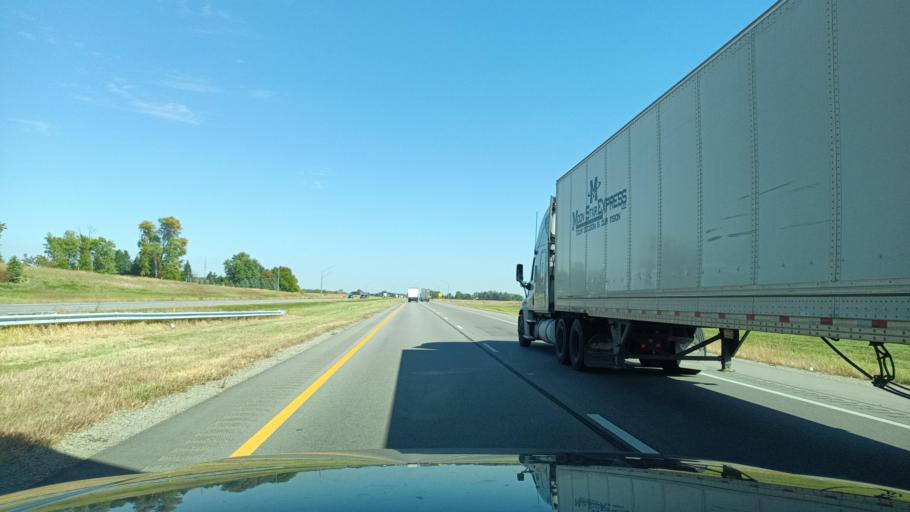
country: US
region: Ohio
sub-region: Defiance County
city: Defiance
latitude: 41.3116
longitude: -84.3236
